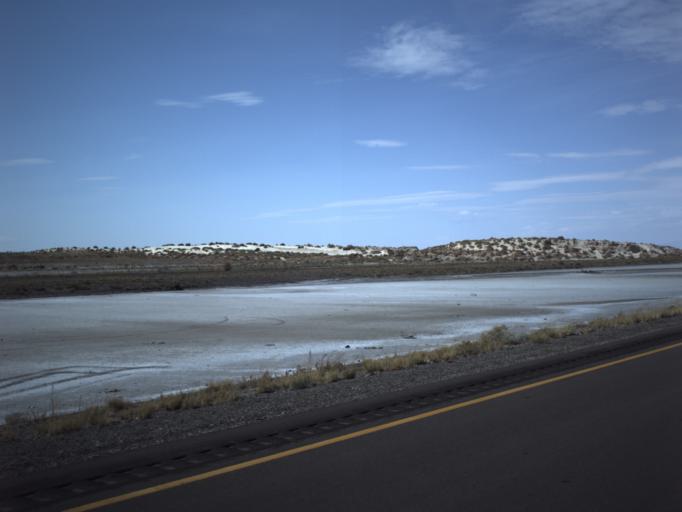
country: US
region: Utah
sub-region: Tooele County
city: Wendover
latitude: 40.7275
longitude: -113.2747
